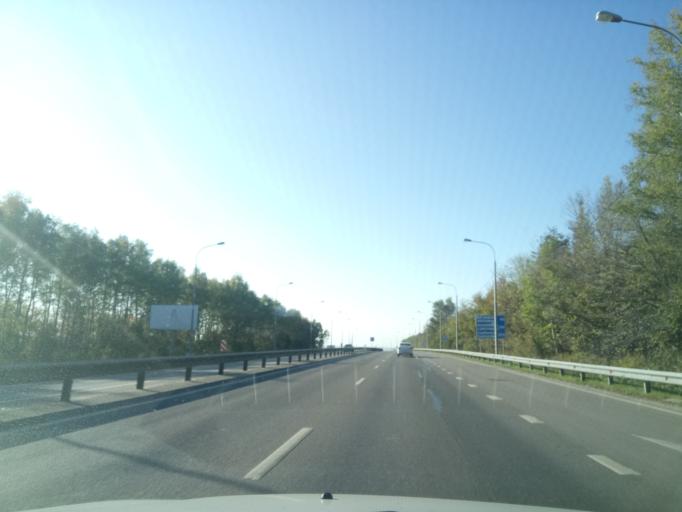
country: RU
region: Nizjnij Novgorod
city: Nizhniy Novgorod
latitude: 56.2078
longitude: 43.9272
